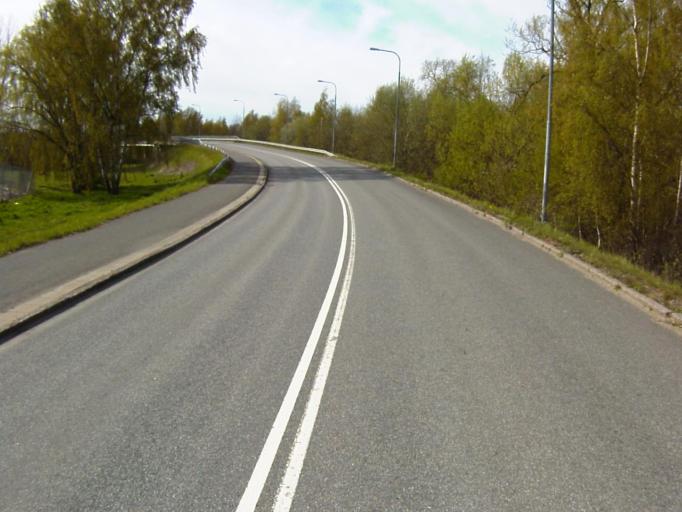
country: SE
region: Skane
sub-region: Kristianstads Kommun
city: Kristianstad
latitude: 56.0192
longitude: 14.1521
